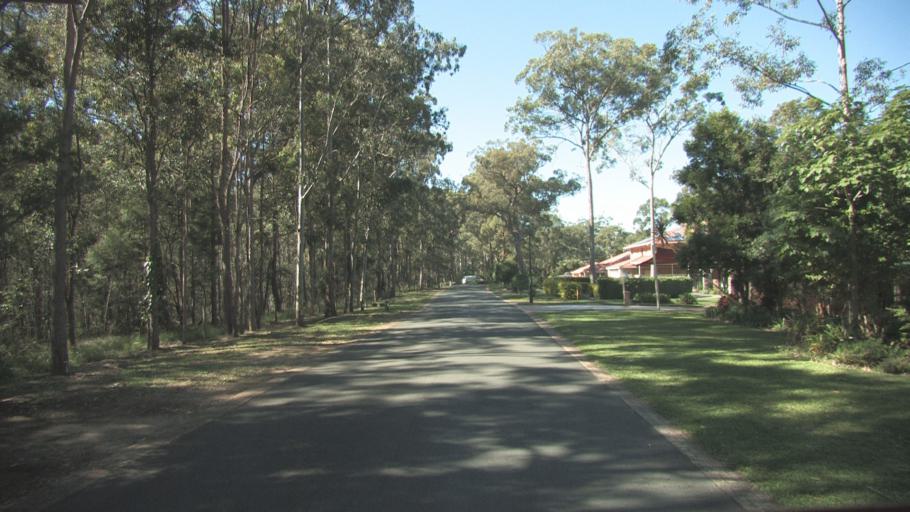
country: AU
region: Queensland
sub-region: Logan
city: Slacks Creek
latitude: -27.6394
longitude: 153.1857
